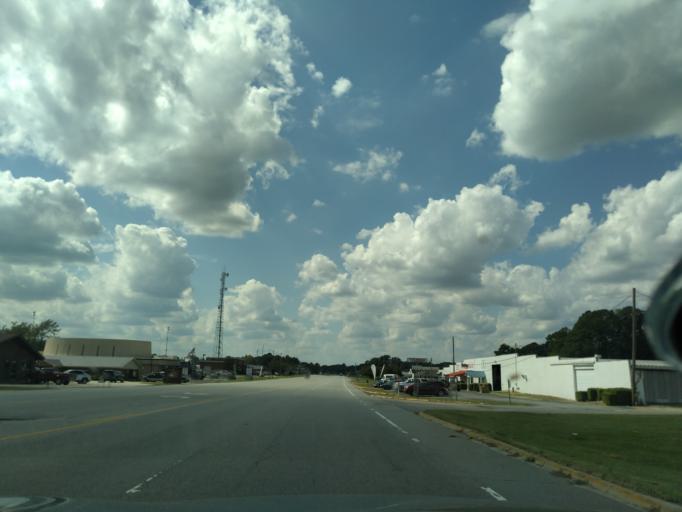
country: US
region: North Carolina
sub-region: Martin County
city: Williamston
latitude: 35.8416
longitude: -77.0653
